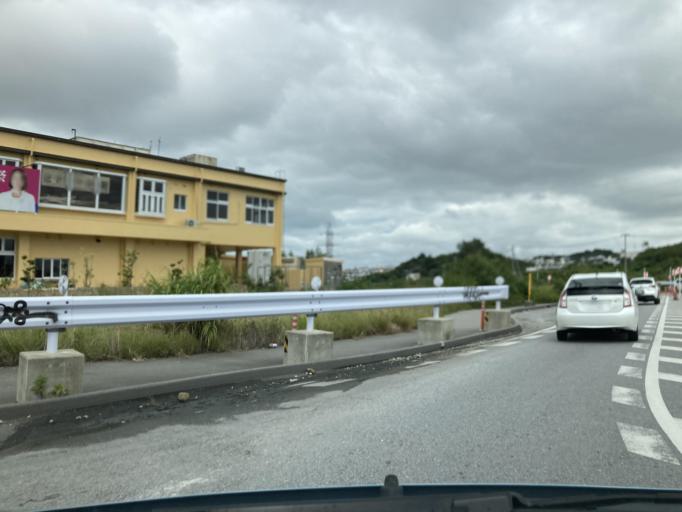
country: JP
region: Okinawa
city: Ginowan
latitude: 26.2396
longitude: 127.7450
